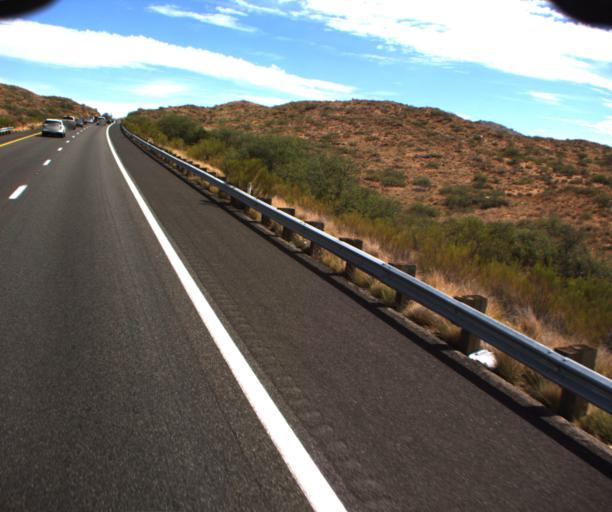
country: US
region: Arizona
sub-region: Yavapai County
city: Cordes Lakes
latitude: 34.2545
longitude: -112.1123
